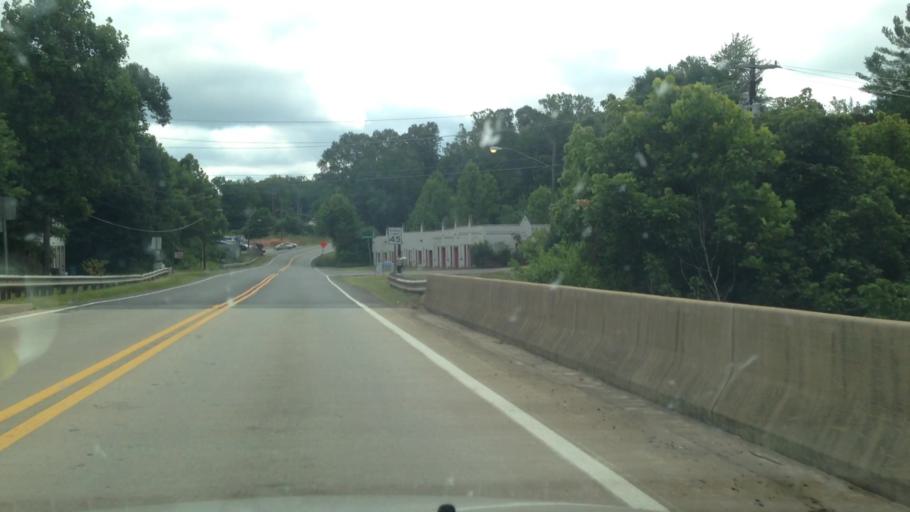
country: US
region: North Carolina
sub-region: Rockingham County
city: Madison
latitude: 36.3850
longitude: -79.9541
